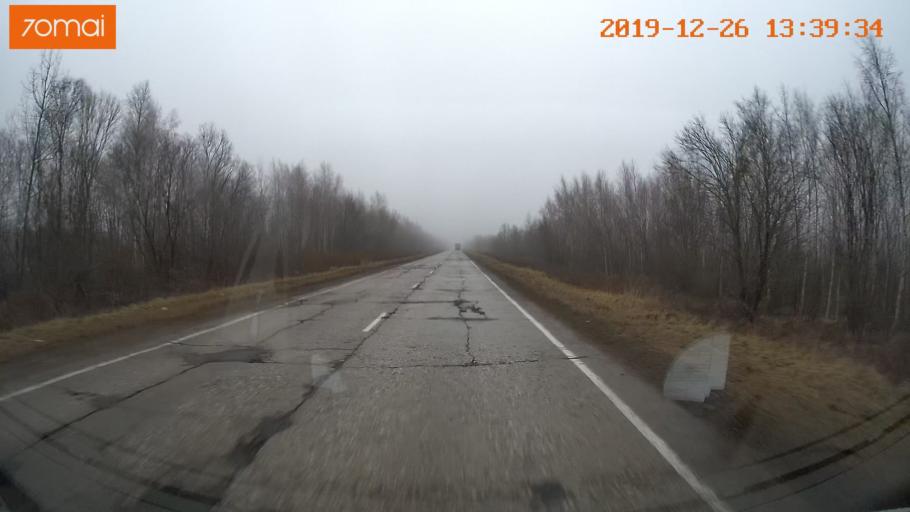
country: RU
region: Vologda
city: Sheksna
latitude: 58.7507
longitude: 38.4139
